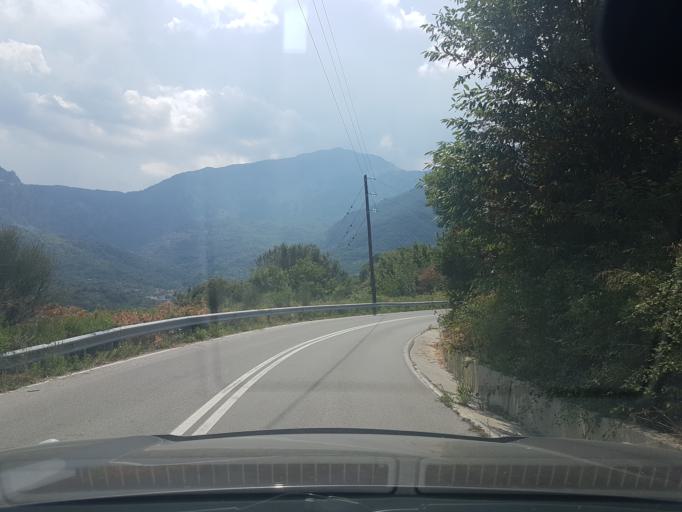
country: GR
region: Central Greece
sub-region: Nomos Evvoias
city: Kymi
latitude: 38.6377
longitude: 23.9451
